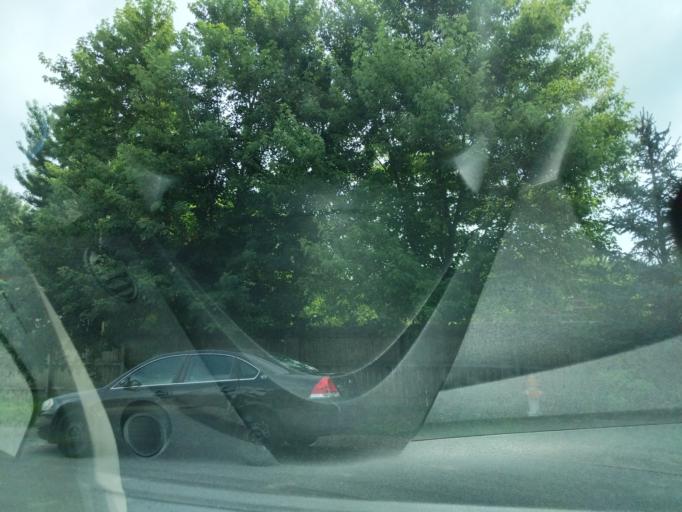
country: US
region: Tennessee
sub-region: Davidson County
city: Lakewood
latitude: 36.1882
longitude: -86.6057
